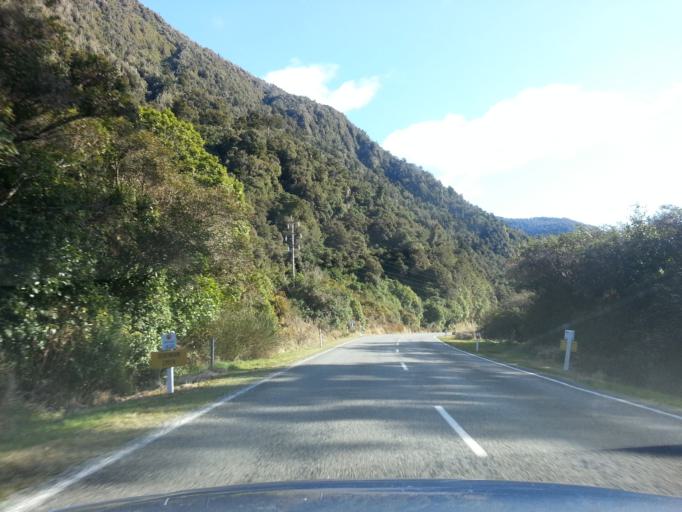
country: NZ
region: West Coast
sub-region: Grey District
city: Greymouth
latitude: -42.7439
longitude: 171.4796
